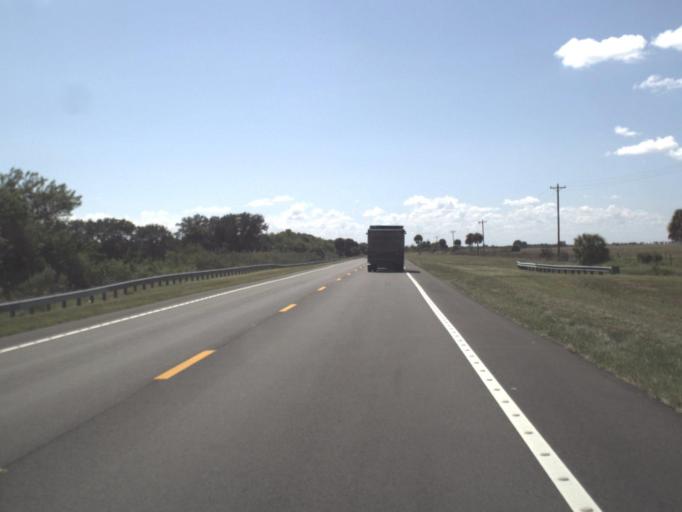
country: US
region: Florida
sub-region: Glades County
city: Buckhead Ridge
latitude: 27.0341
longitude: -81.0025
